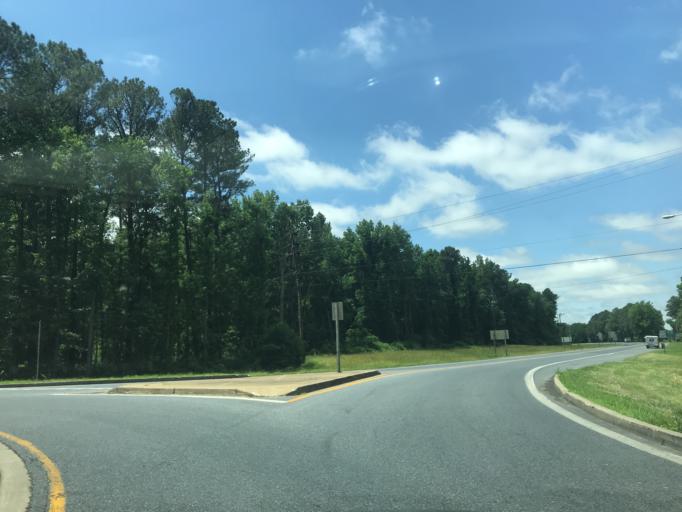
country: US
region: Maryland
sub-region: Caroline County
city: Federalsburg
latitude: 38.6895
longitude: -75.7896
